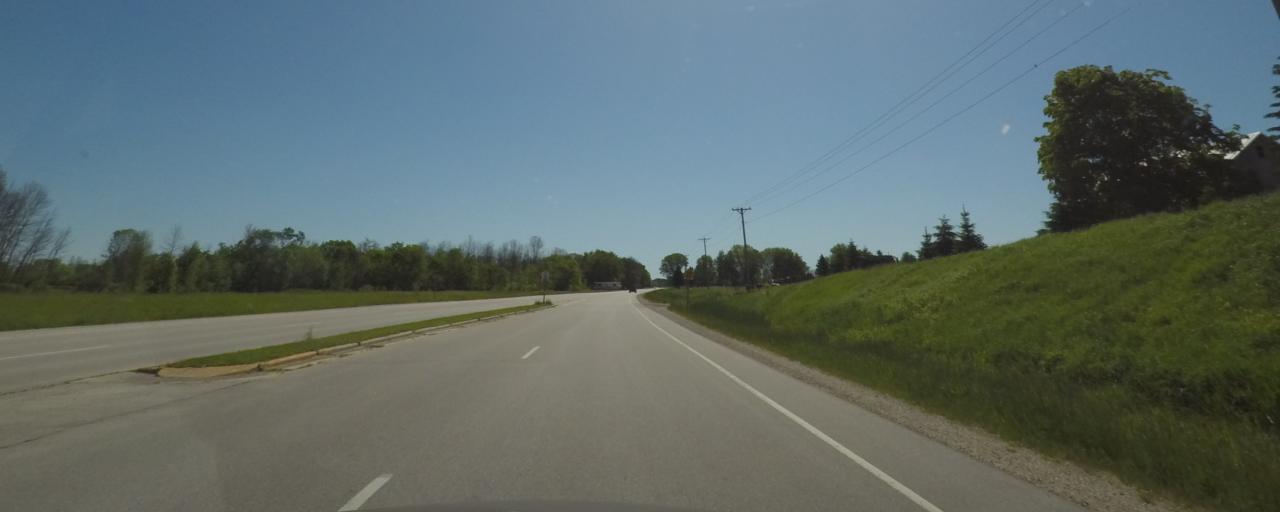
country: US
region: Wisconsin
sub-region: Sheboygan County
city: Plymouth
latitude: 43.7471
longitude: -87.9366
